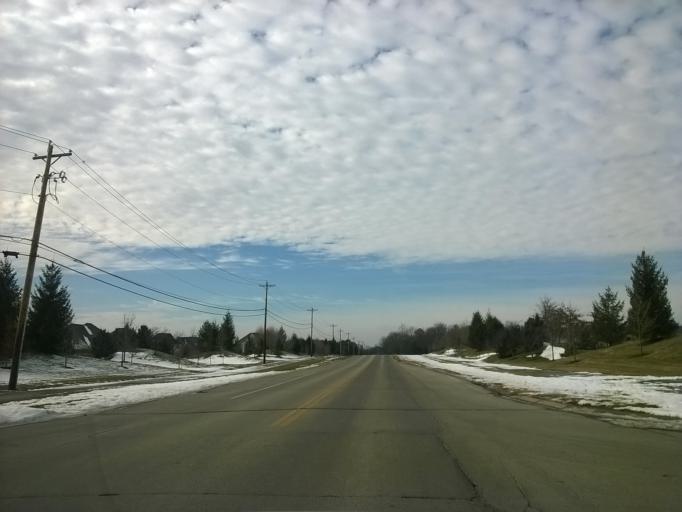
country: US
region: Indiana
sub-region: Boone County
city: Zionsville
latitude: 39.9772
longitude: -86.2271
